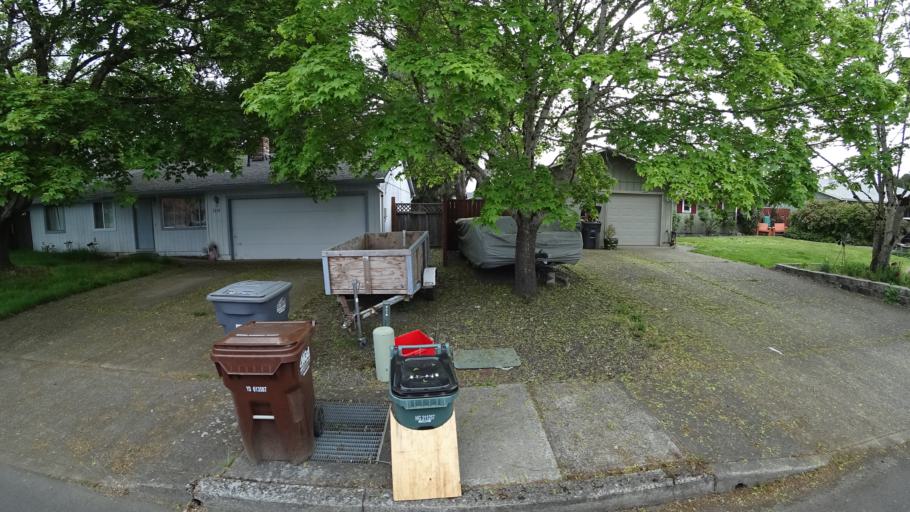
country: US
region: Oregon
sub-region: Washington County
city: Hillsboro
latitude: 45.5382
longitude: -122.9696
